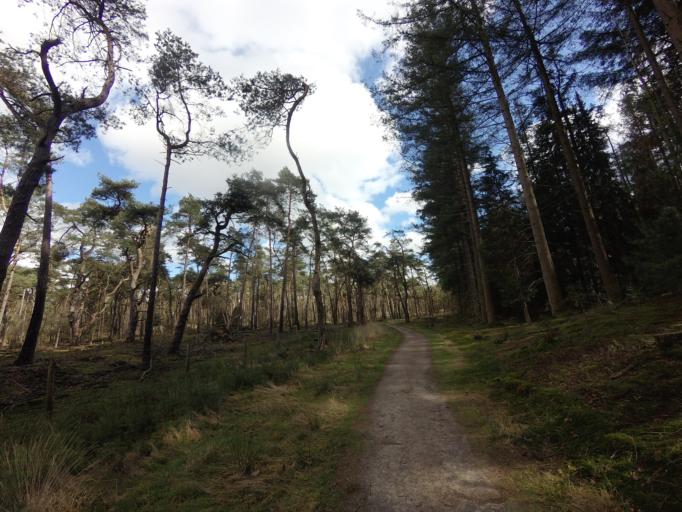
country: NL
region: Utrecht
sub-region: Gemeente Utrechtse Heuvelrug
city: Driebergen-Rijsenburg
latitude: 52.0734
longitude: 5.2970
